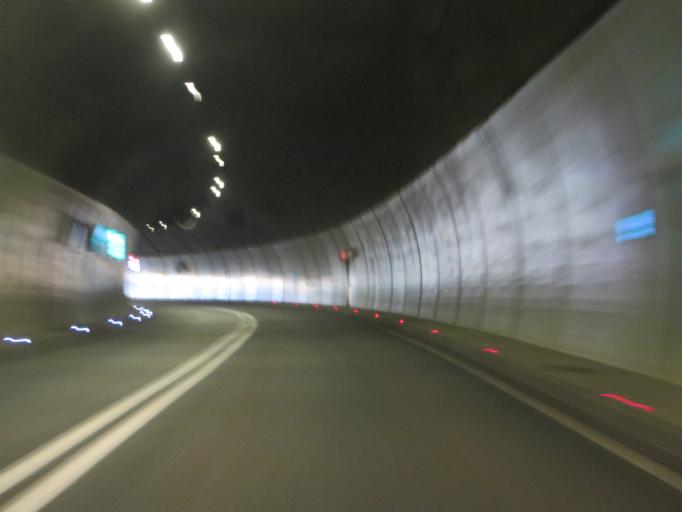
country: IT
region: Trentino-Alto Adige
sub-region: Bolzano
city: Ora
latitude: 46.3458
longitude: 11.3074
